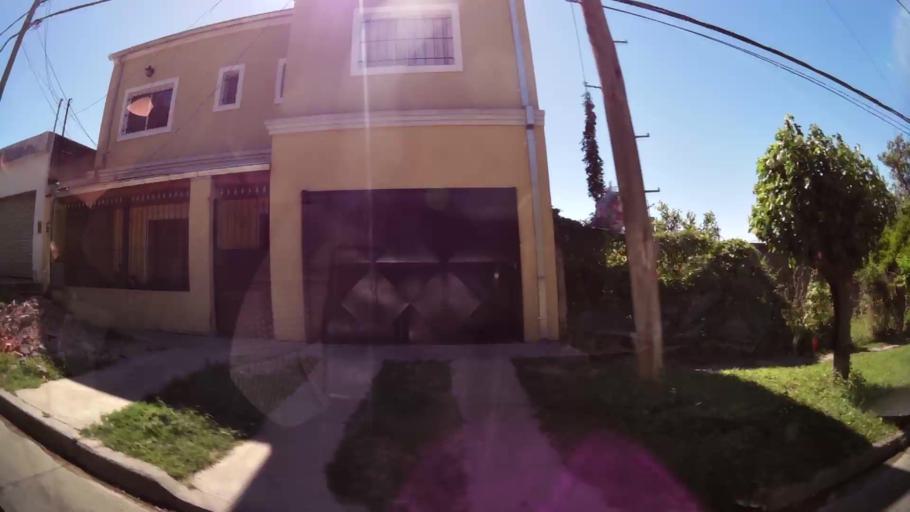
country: AR
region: Buenos Aires
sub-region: Partido de Tigre
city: Tigre
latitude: -34.5027
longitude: -58.6140
